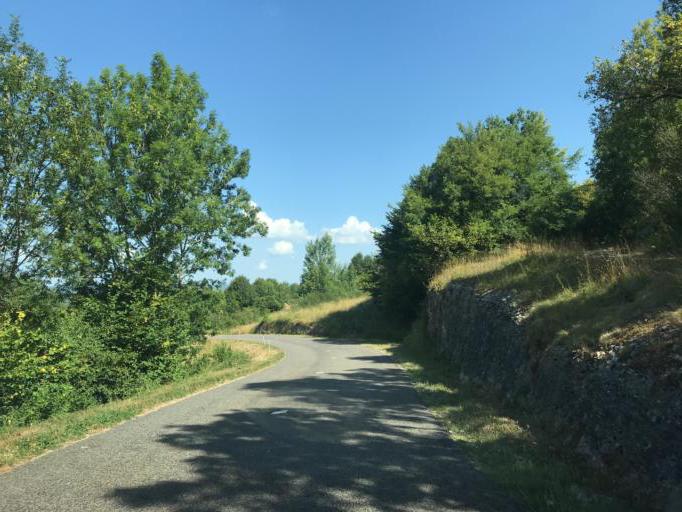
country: FR
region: Franche-Comte
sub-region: Departement du Jura
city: Moirans-en-Montagne
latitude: 46.4593
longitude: 5.7327
